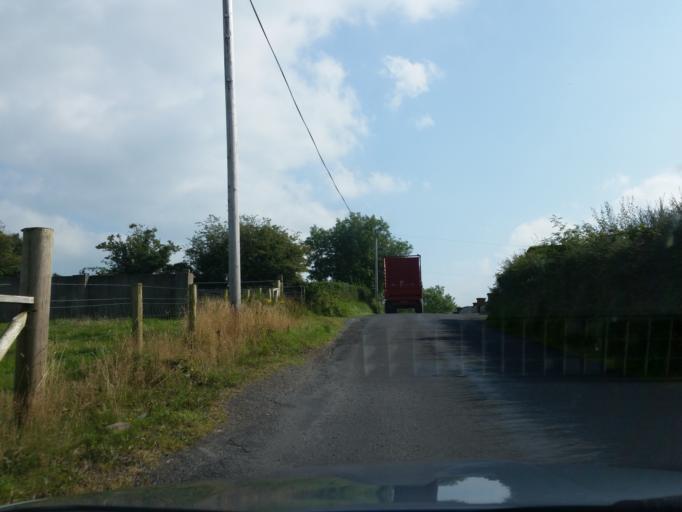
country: GB
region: Northern Ireland
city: Ballinamallard
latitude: 54.3390
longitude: -7.5380
